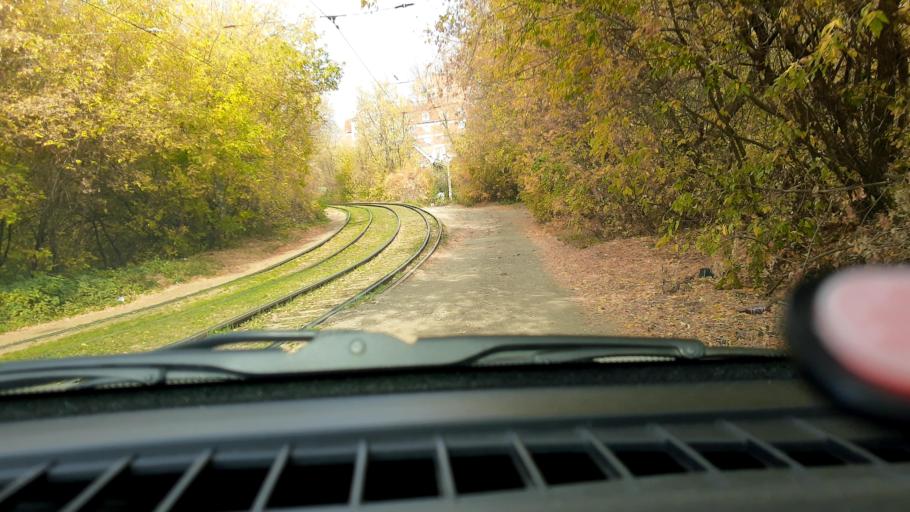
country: RU
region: Nizjnij Novgorod
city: Nizhniy Novgorod
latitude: 56.2946
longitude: 43.9944
